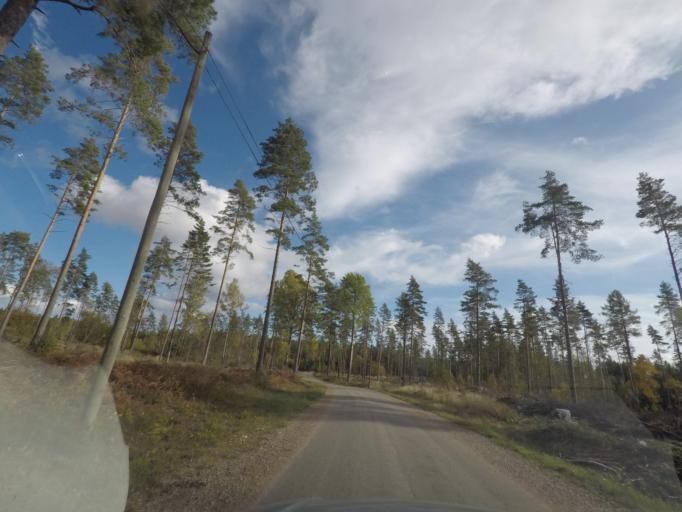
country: SE
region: Vaestmanland
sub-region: Kungsors Kommun
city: Kungsoer
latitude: 59.3376
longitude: 16.2096
